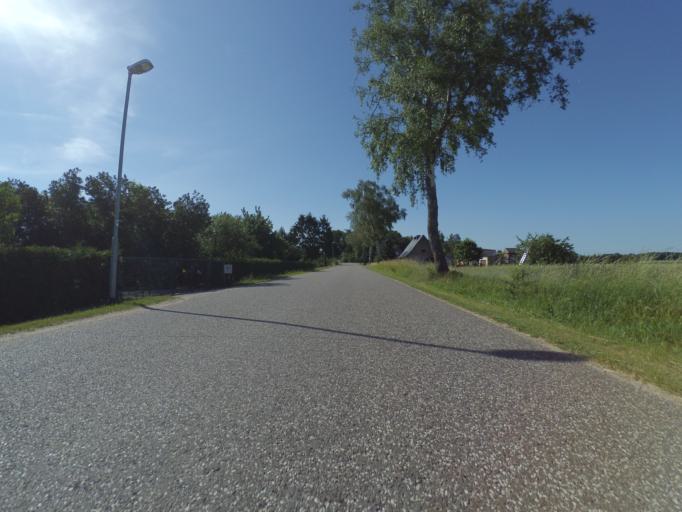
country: DE
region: Brandenburg
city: Putlitz
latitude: 53.2740
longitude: 12.0912
